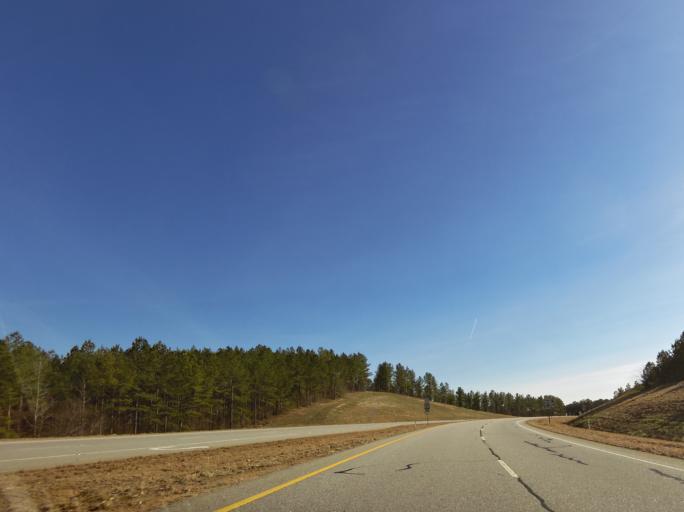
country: US
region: Georgia
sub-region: Upson County
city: Thomaston
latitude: 32.7407
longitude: -84.2185
